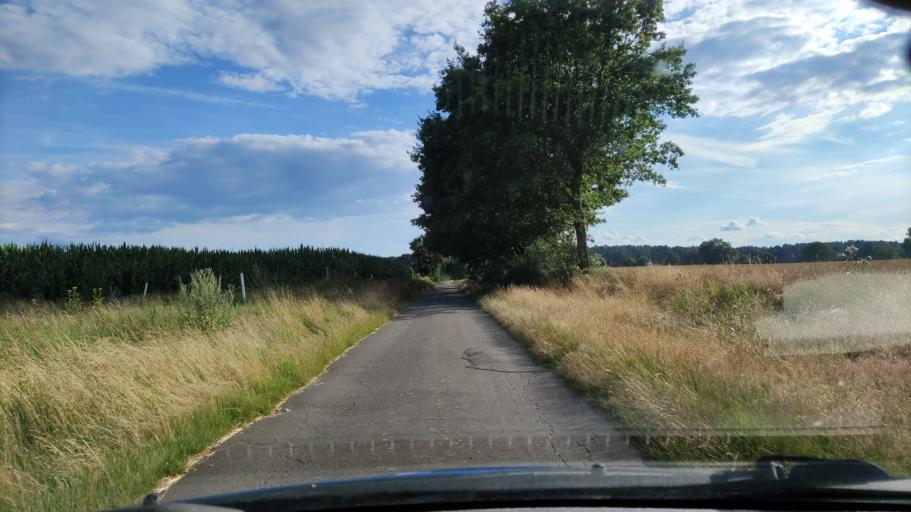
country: DE
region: Lower Saxony
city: Boitze
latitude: 53.1447
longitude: 10.7422
